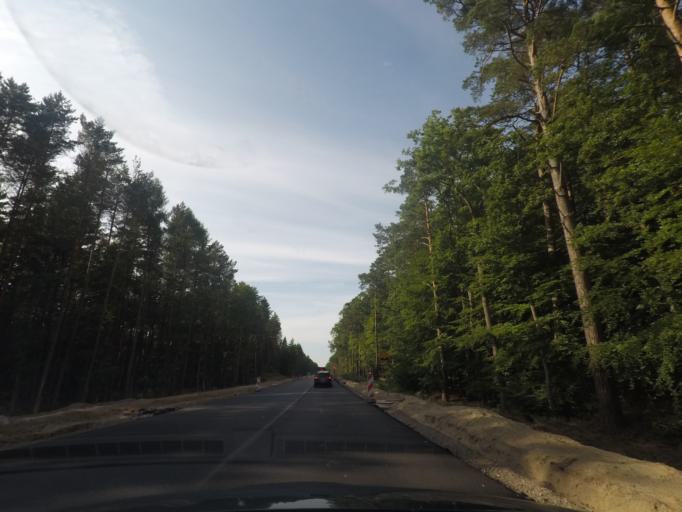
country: PL
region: Pomeranian Voivodeship
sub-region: Powiat leborski
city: Leba
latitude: 54.6998
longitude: 17.5880
